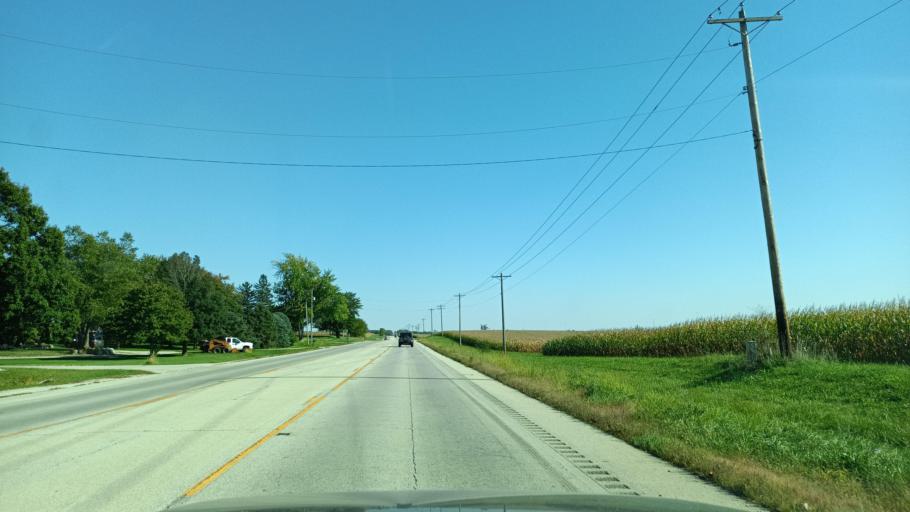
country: US
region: Illinois
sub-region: Champaign County
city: Lake of the Woods
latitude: 40.1808
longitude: -88.3573
